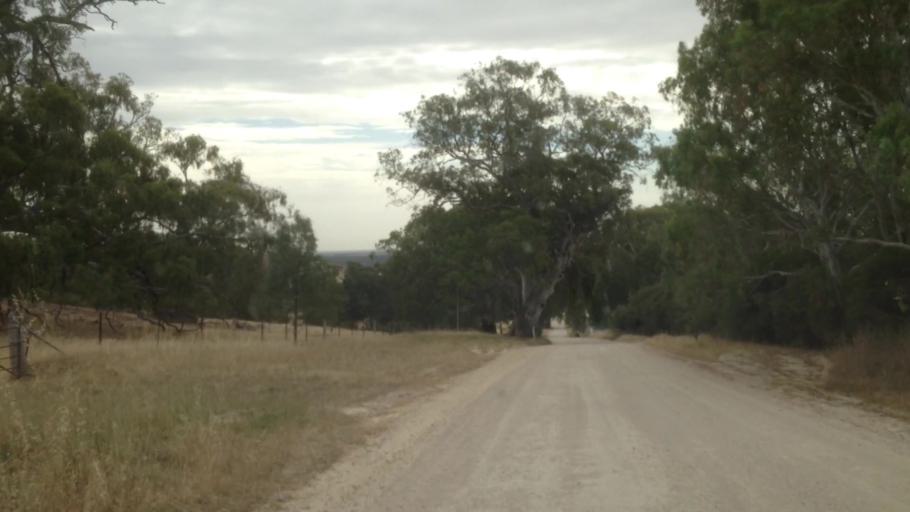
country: AU
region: South Australia
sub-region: Barossa
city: Lyndoch
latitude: -34.5996
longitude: 138.9426
